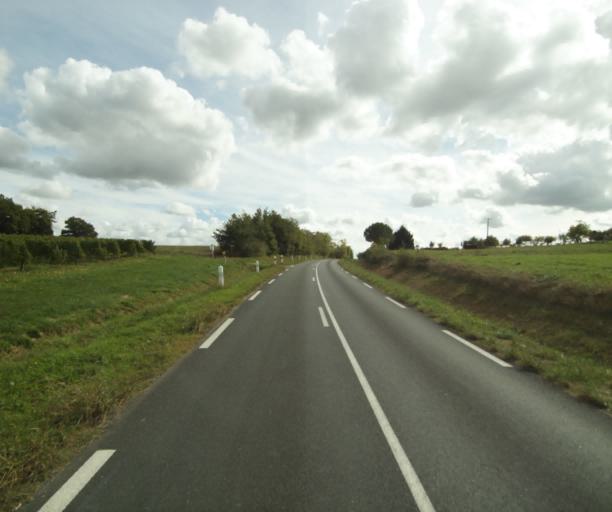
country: FR
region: Midi-Pyrenees
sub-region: Departement du Gers
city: Eauze
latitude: 43.8270
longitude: 0.0945
